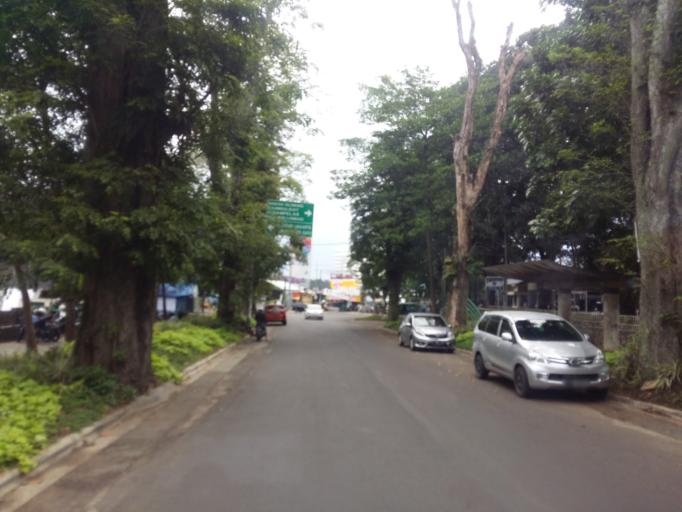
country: ID
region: West Java
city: Bandung
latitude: -6.8935
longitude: 107.6092
